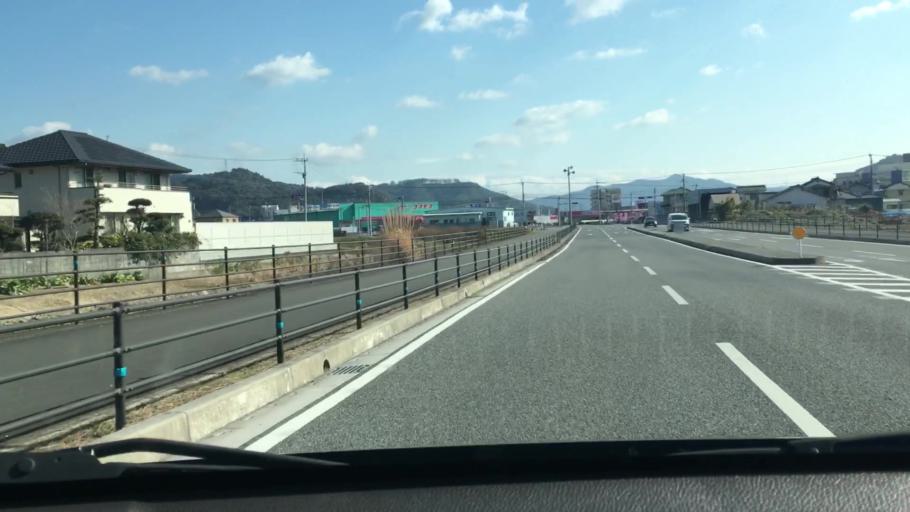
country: JP
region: Oita
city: Saiki
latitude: 32.9614
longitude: 131.8595
